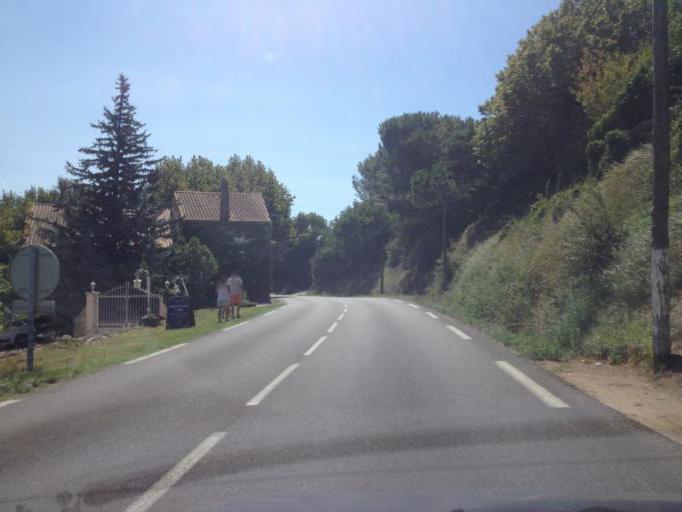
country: FR
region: Languedoc-Roussillon
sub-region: Departement du Gard
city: Sauveterre
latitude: 44.0145
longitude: 4.7973
